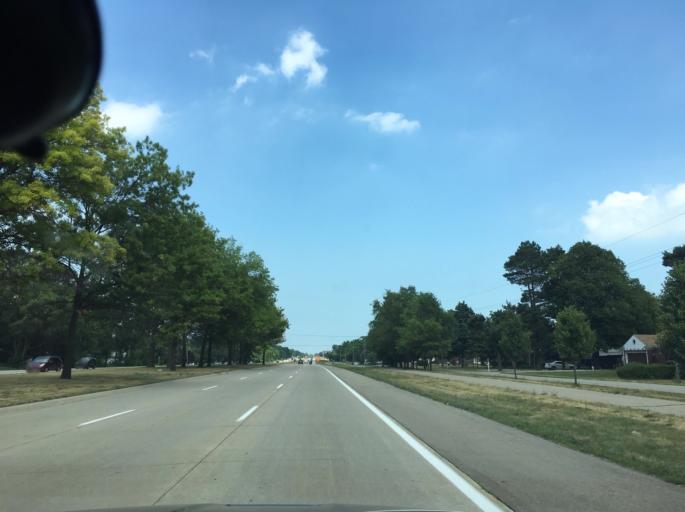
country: US
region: Michigan
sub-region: Macomb County
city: Clinton
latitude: 42.5684
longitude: -82.9366
